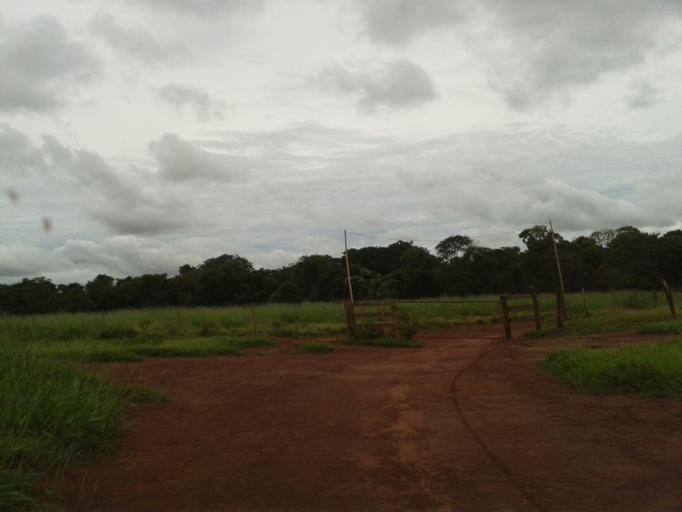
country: BR
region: Minas Gerais
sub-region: Capinopolis
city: Capinopolis
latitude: -18.7855
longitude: -49.7807
